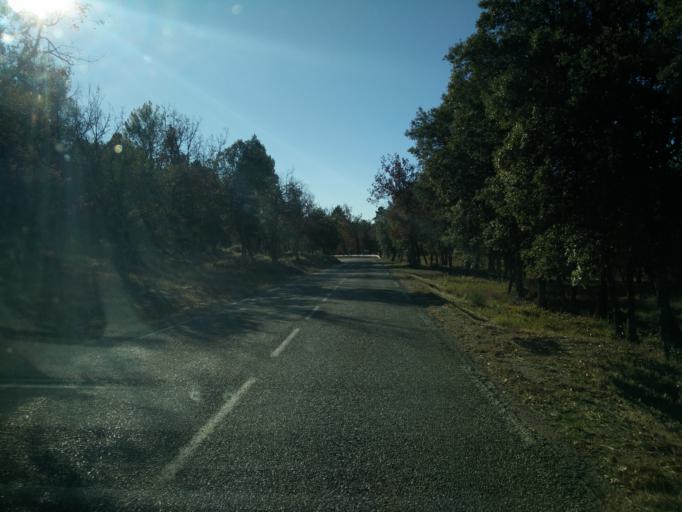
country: FR
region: Provence-Alpes-Cote d'Azur
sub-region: Departement du Var
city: Aups
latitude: 43.6036
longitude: 6.2195
